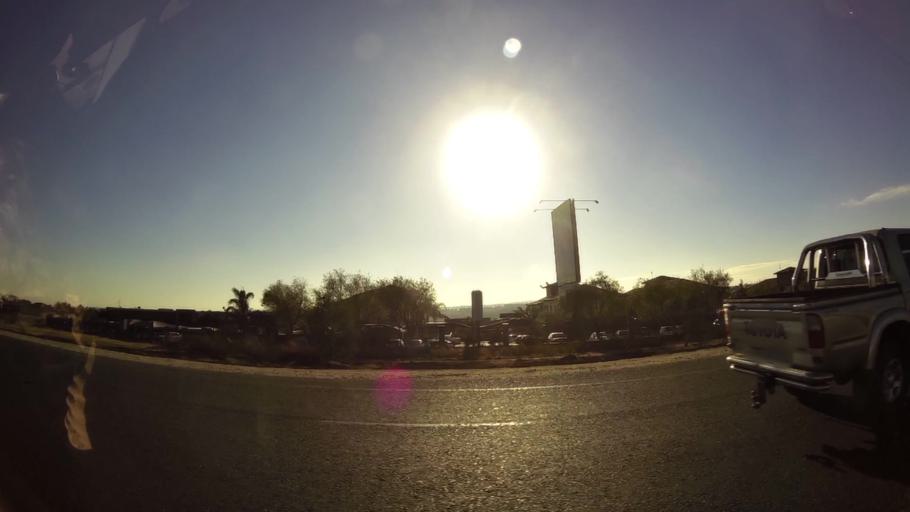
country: ZA
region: Gauteng
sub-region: City of Johannesburg Metropolitan Municipality
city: Roodepoort
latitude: -26.0991
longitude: 27.8758
